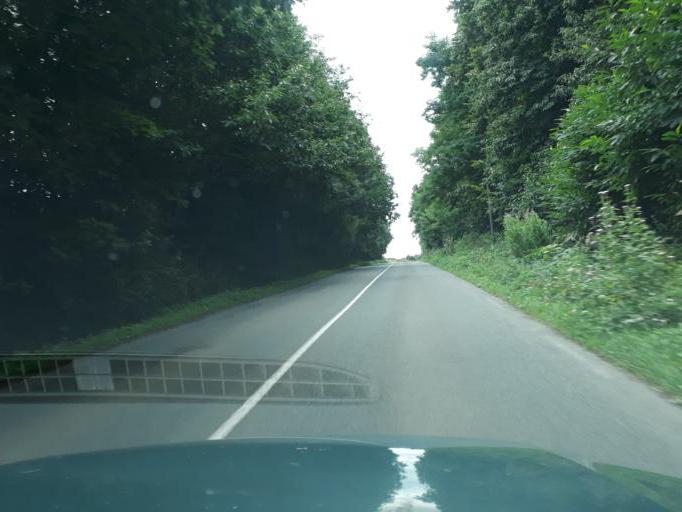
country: FR
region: Brittany
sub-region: Departement des Cotes-d'Armor
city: Plehedel
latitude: 48.6860
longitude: -3.0197
